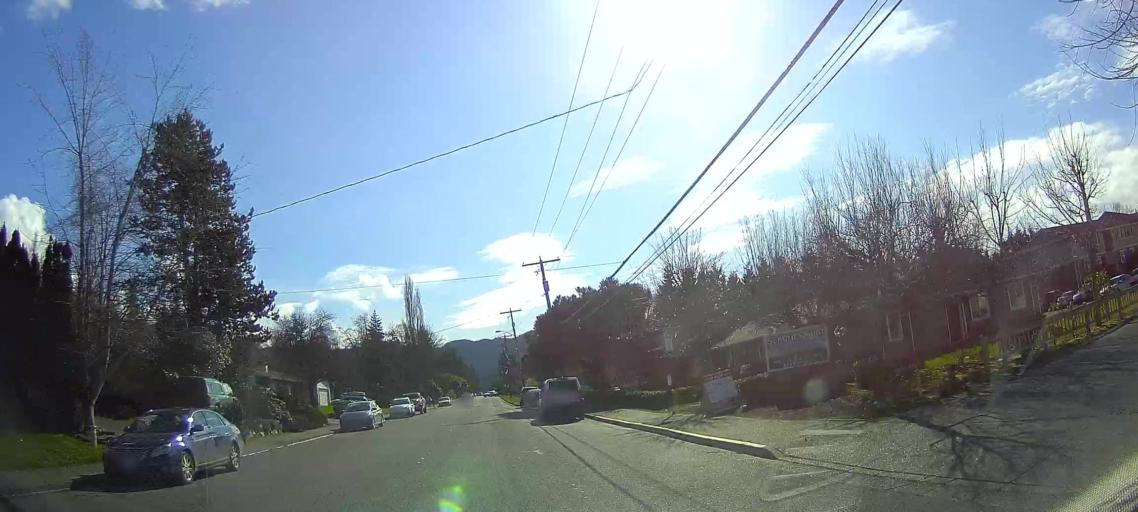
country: US
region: Washington
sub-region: Whatcom County
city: Bellingham
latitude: 48.7265
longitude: -122.4754
